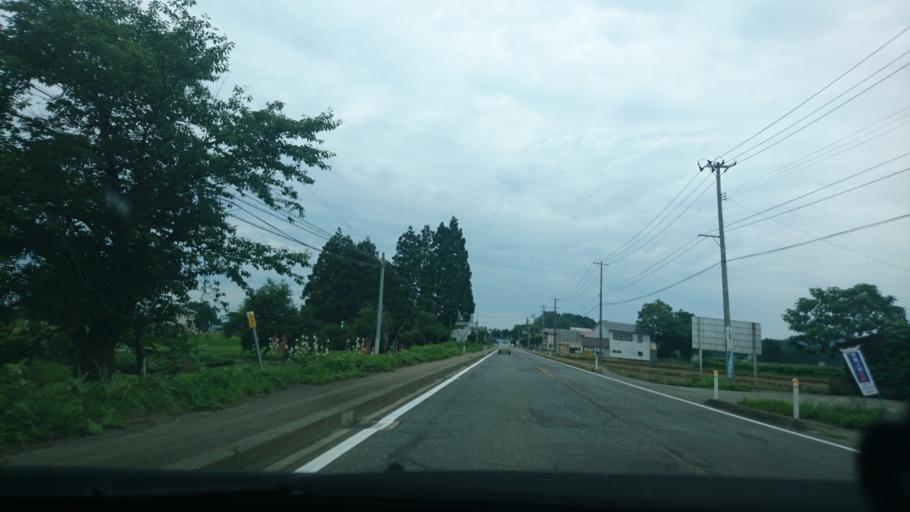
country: JP
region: Akita
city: Yokotemachi
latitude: 39.3493
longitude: 140.5620
